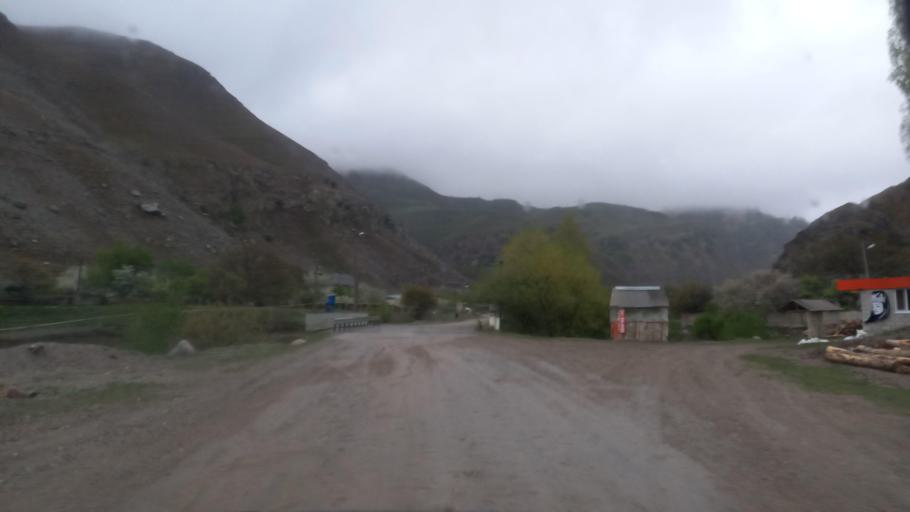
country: RU
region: Kabardino-Balkariya
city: Bylym
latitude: 43.4471
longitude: 43.0310
